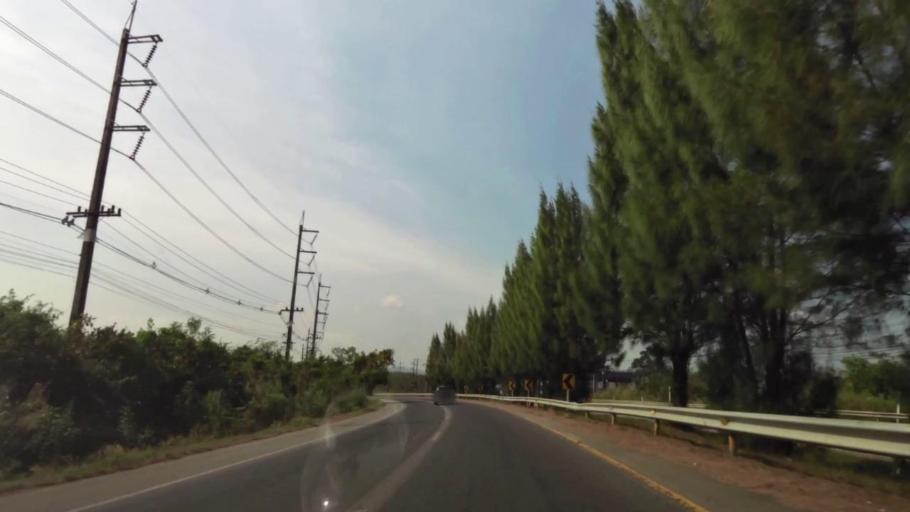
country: TH
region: Chanthaburi
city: Chanthaburi
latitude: 12.6629
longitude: 102.1199
